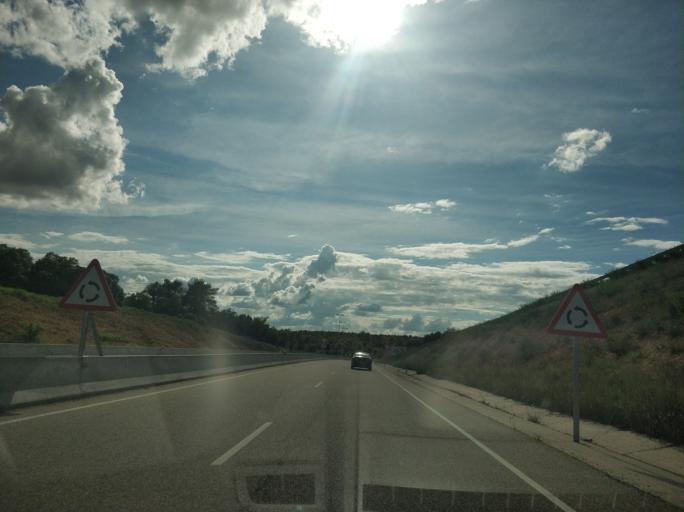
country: ES
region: Castille and Leon
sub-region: Provincia de Burgos
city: Aranda de Duero
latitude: 41.6992
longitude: -3.6809
